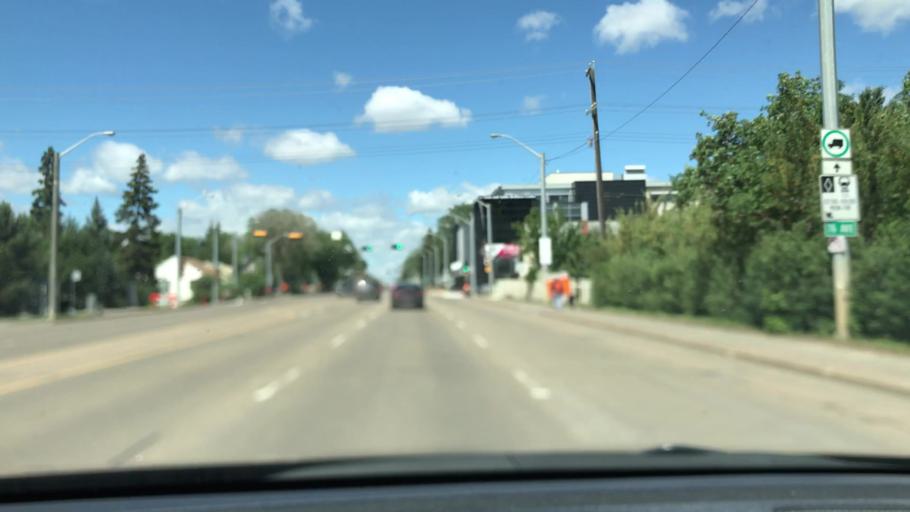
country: CA
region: Alberta
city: Edmonton
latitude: 53.5114
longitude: -113.5118
